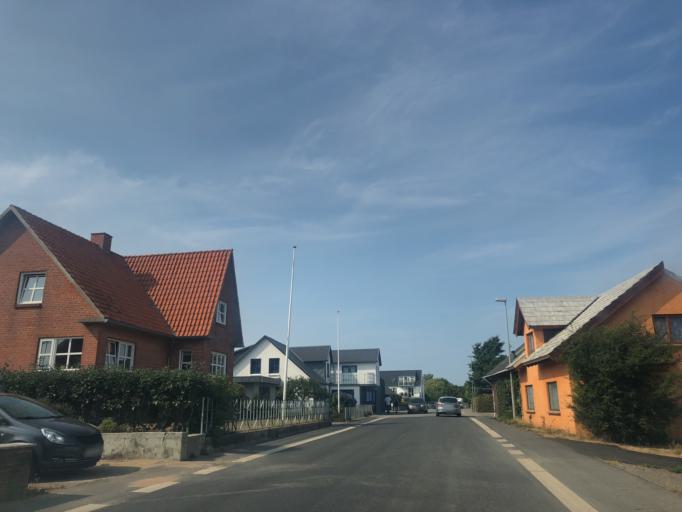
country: DK
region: North Denmark
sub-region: Morso Kommune
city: Nykobing Mors
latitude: 56.8052
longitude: 9.0203
